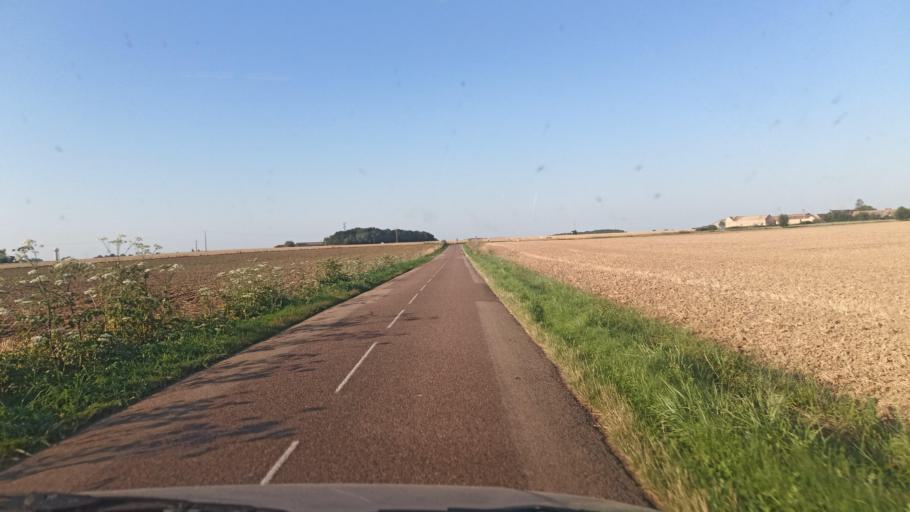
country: FR
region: Bourgogne
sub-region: Departement de l'Yonne
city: Saint-Valerien
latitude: 48.2119
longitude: 3.1208
